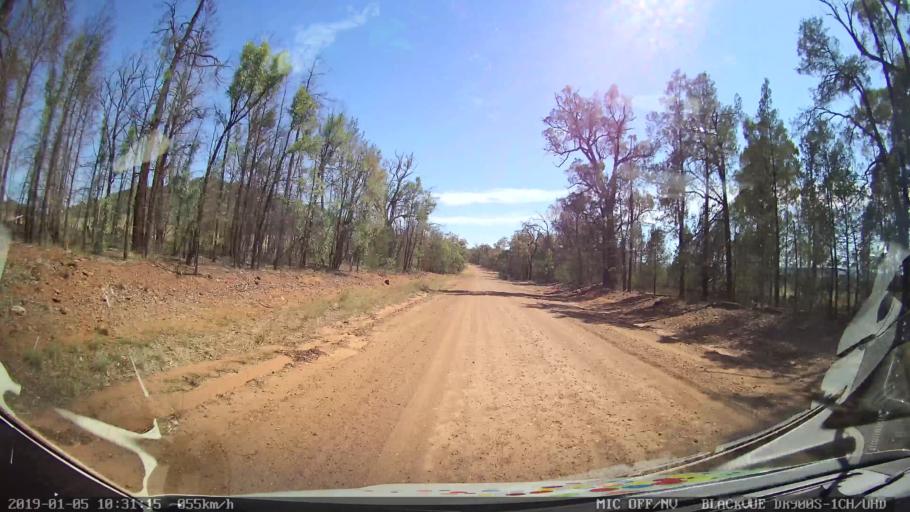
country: AU
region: New South Wales
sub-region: Gilgandra
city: Gilgandra
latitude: -31.5258
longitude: 148.9272
